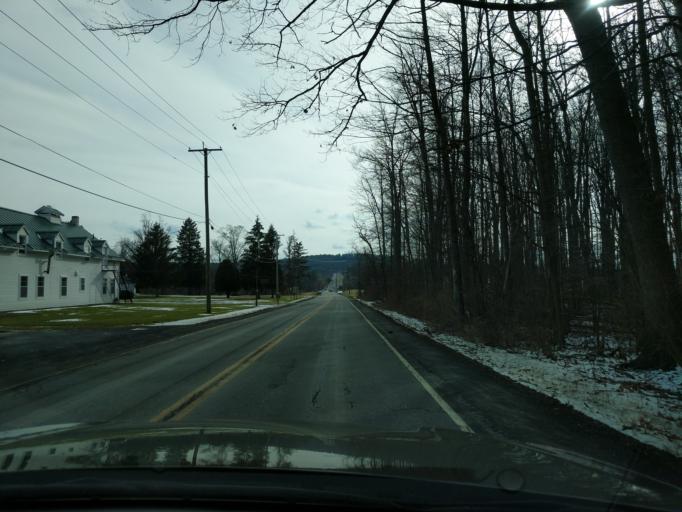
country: US
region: New York
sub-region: Tompkins County
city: Northeast Ithaca
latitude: 42.4460
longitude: -76.4491
